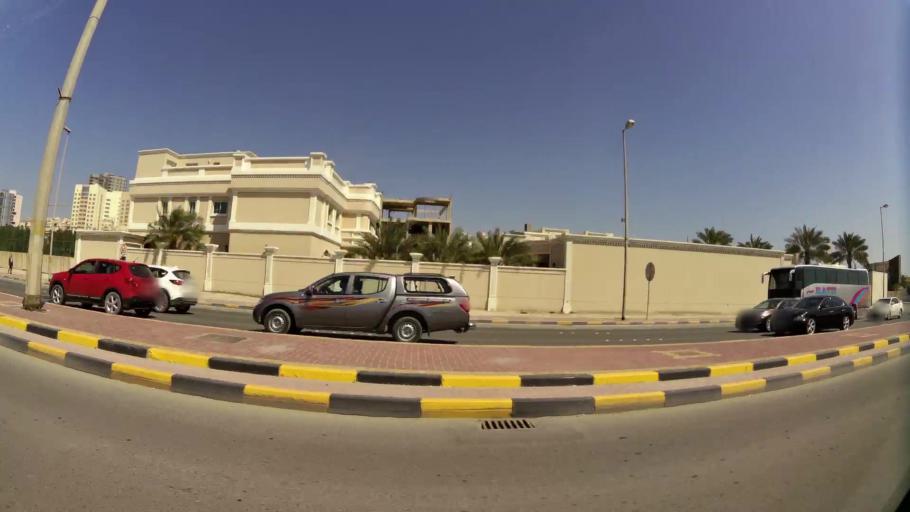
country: BH
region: Manama
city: Manama
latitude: 26.2096
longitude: 50.5974
